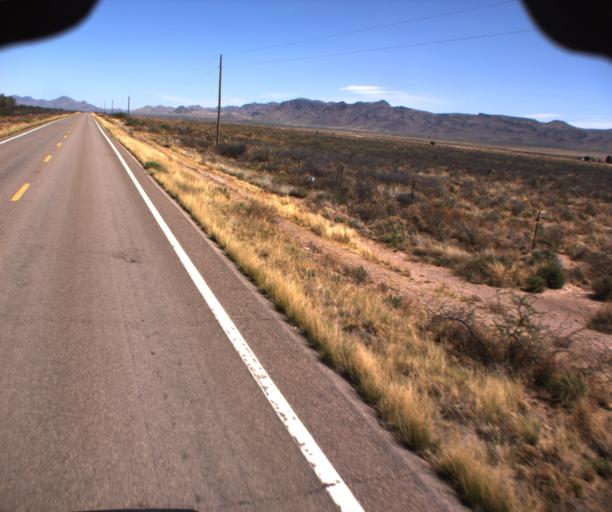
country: US
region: Arizona
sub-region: Cochise County
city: Douglas
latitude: 31.7588
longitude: -109.0854
